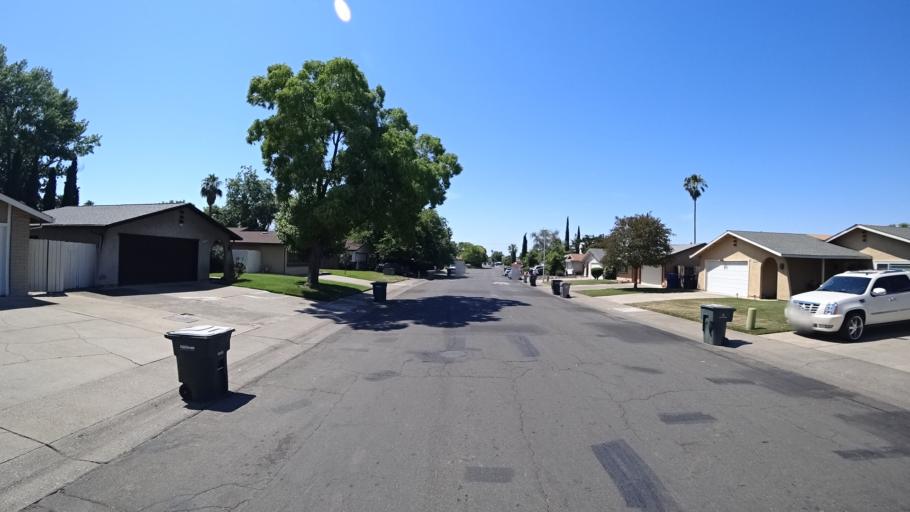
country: US
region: California
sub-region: Sacramento County
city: Florin
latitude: 38.5340
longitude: -121.4144
